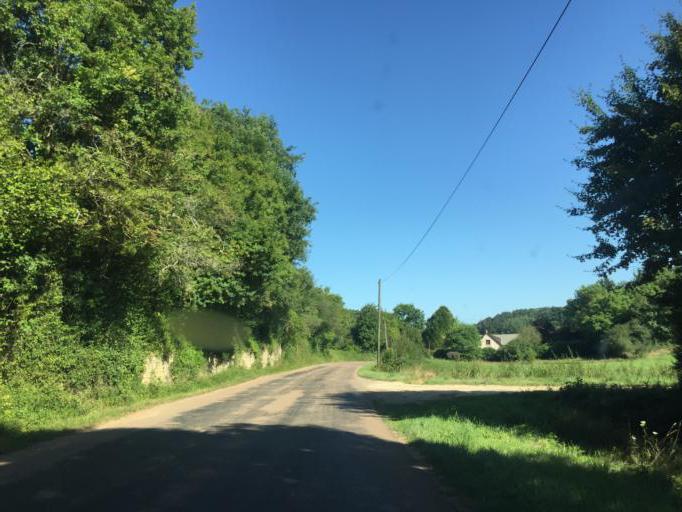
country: FR
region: Bourgogne
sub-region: Departement de l'Yonne
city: Fontenailles
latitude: 47.4818
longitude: 3.4060
